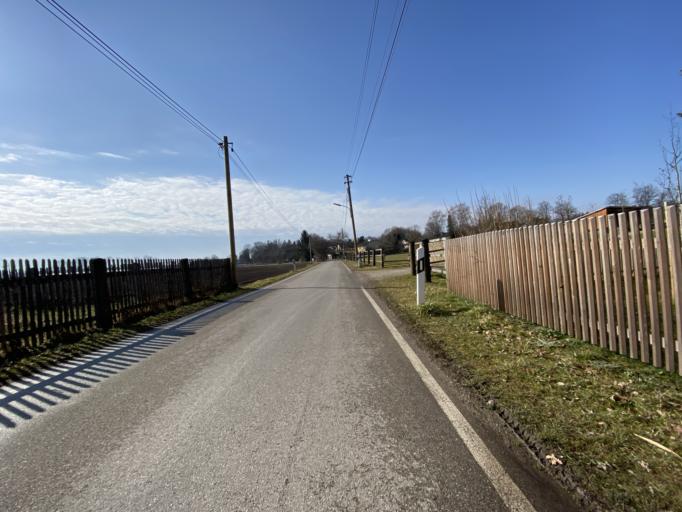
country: DE
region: Bavaria
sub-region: Upper Bavaria
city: Unterfoehring
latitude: 48.1680
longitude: 11.6491
